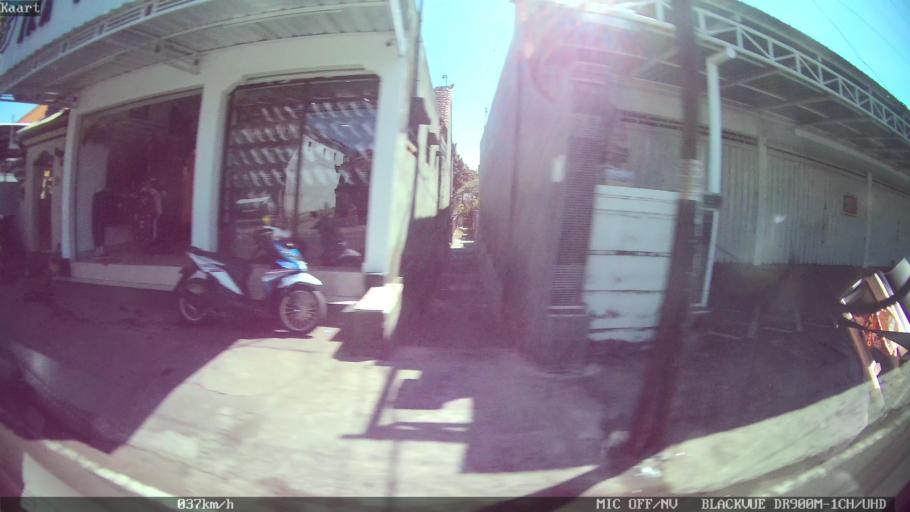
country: ID
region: Bali
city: Banjar Sidayu
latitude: -8.0976
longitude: 115.1183
